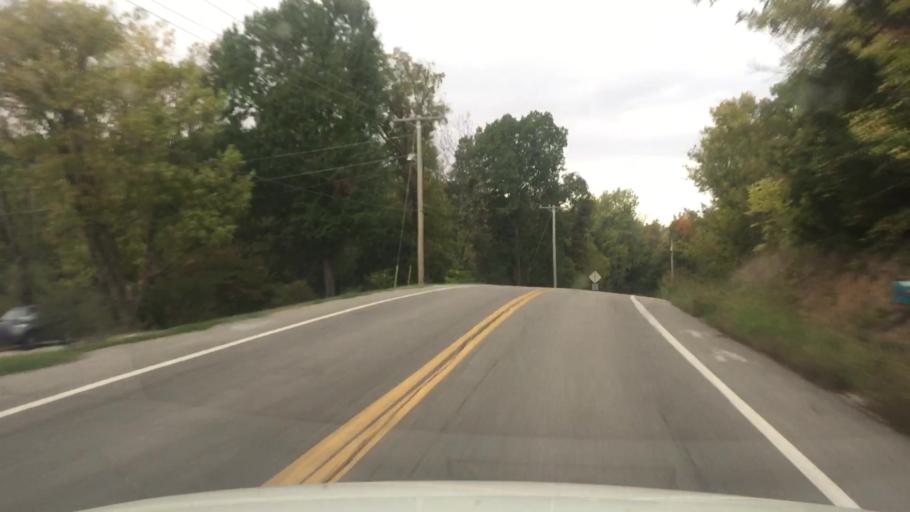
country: US
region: Missouri
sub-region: Boone County
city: Columbia
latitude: 38.8787
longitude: -92.4183
